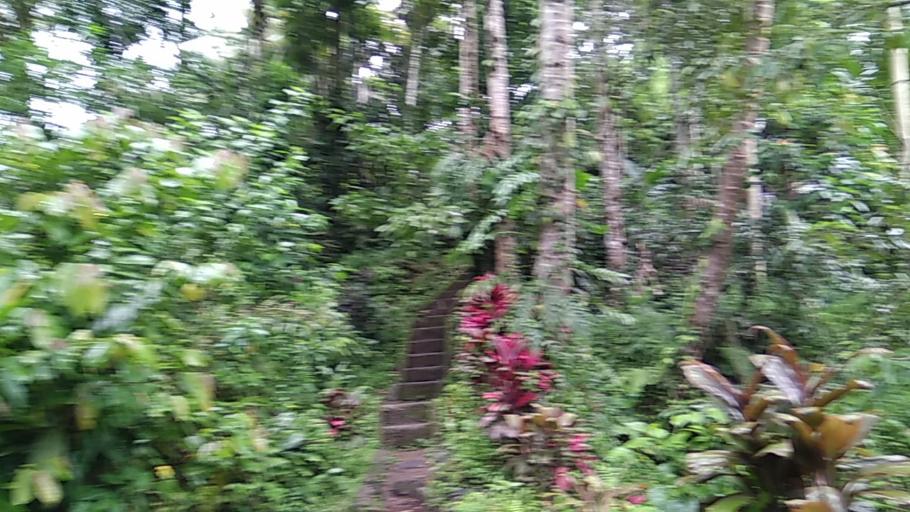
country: ID
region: Bali
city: Banjar Kubu
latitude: -8.4412
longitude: 115.3885
